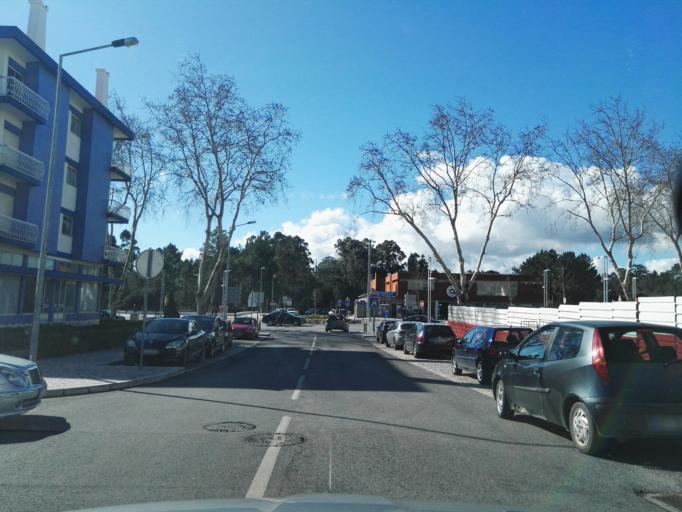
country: PT
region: Santarem
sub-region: Ourem
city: Fatima
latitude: 39.6318
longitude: -8.6795
